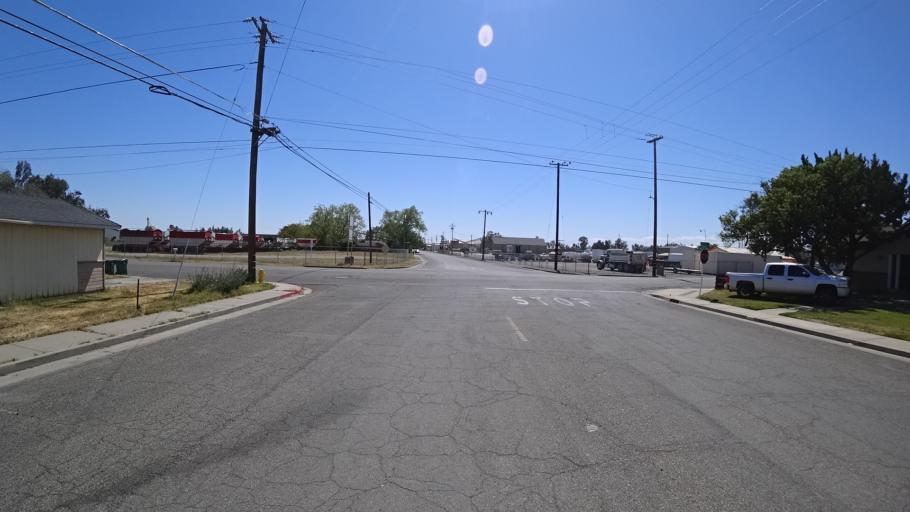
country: US
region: California
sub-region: Glenn County
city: Orland
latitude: 39.7404
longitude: -122.1951
